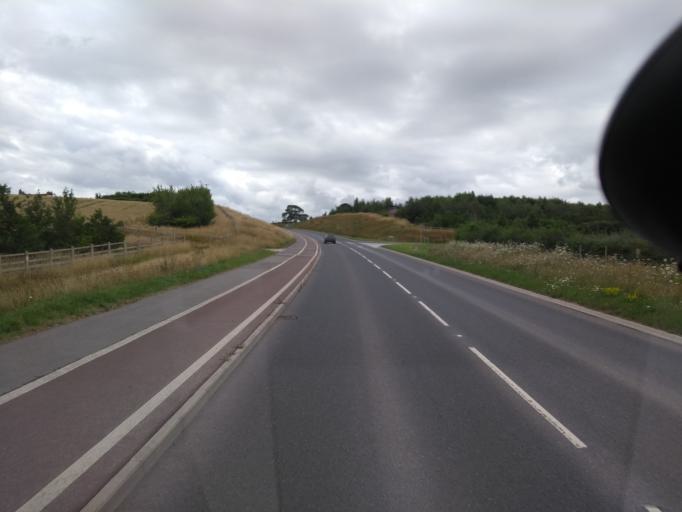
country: GB
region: England
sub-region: Somerset
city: Bridgwater
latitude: 51.1566
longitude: -3.0706
